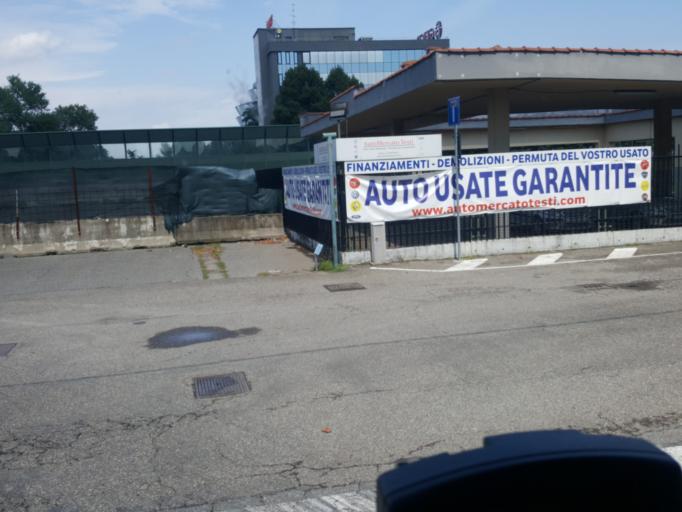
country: IT
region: Lombardy
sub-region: Citta metropolitana di Milano
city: Sesto San Giovanni
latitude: 45.5516
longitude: 9.2439
